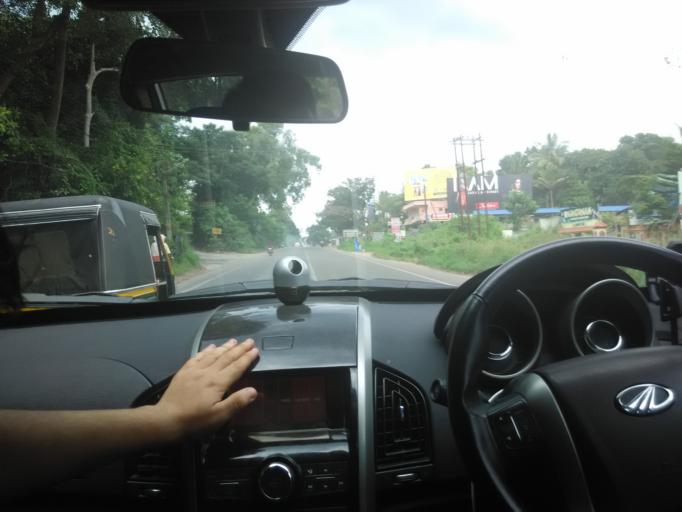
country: IN
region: Kerala
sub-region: Thiruvananthapuram
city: Attingal
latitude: 8.6377
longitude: 76.8457
